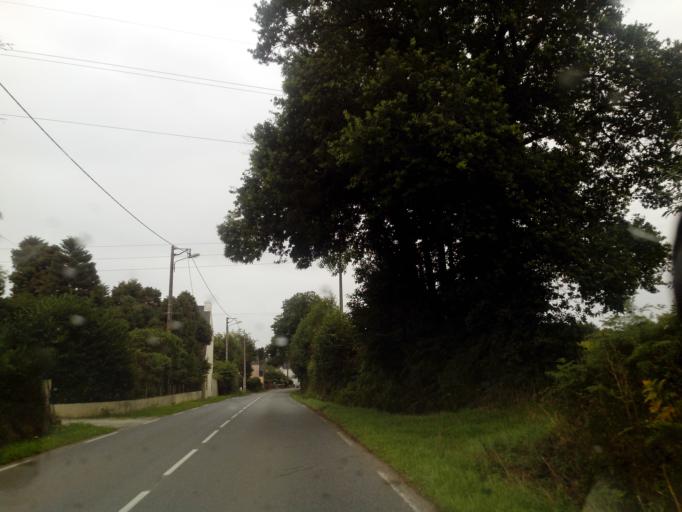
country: FR
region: Brittany
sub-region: Departement du Finistere
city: Tremeven
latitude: 47.8935
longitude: -3.5278
